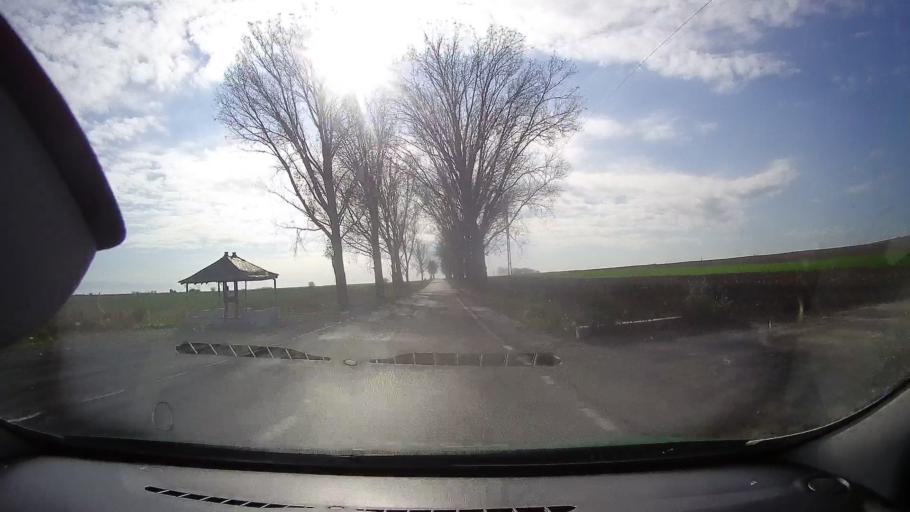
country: RO
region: Tulcea
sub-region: Comuna Valea Nucarilor
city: Agighiol
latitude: 45.0016
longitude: 28.8858
